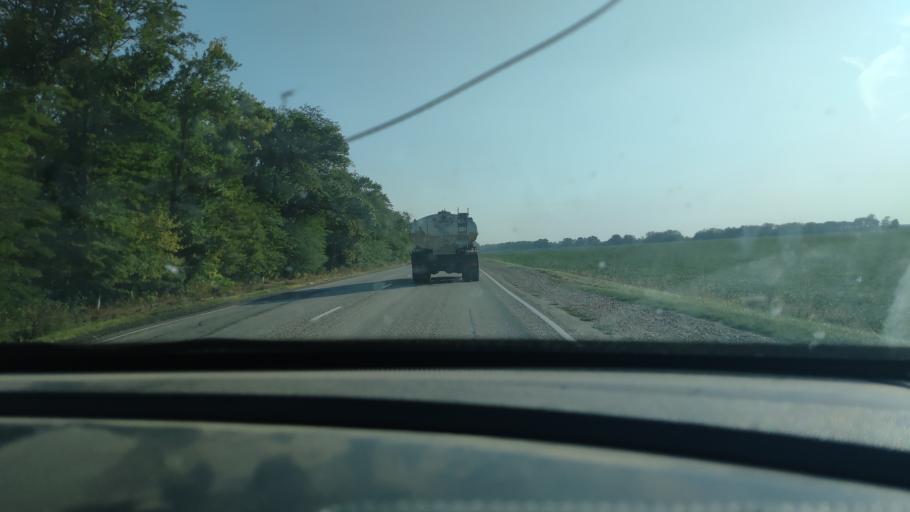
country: RU
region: Krasnodarskiy
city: Starominskaya
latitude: 46.4594
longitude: 39.0361
